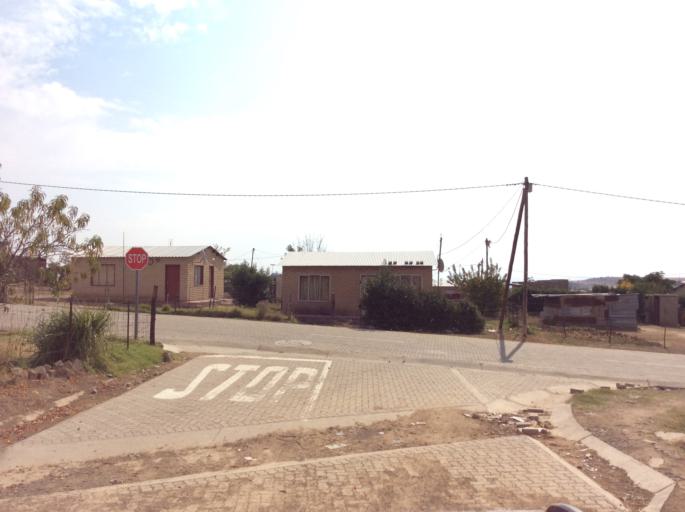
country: ZA
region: Orange Free State
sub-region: Xhariep District Municipality
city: Dewetsdorp
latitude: -29.5937
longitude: 26.6788
